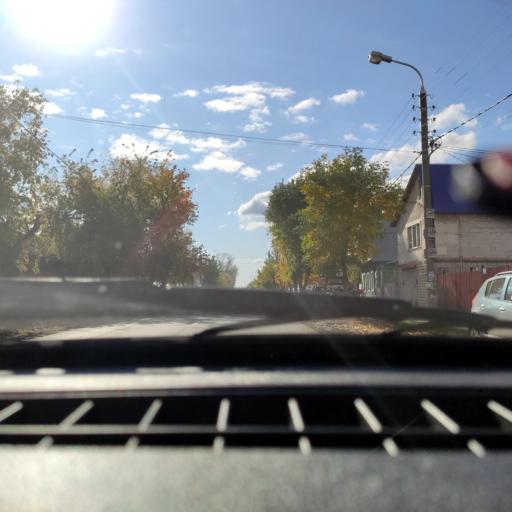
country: RU
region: Bashkortostan
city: Ufa
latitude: 54.7362
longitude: 55.9194
